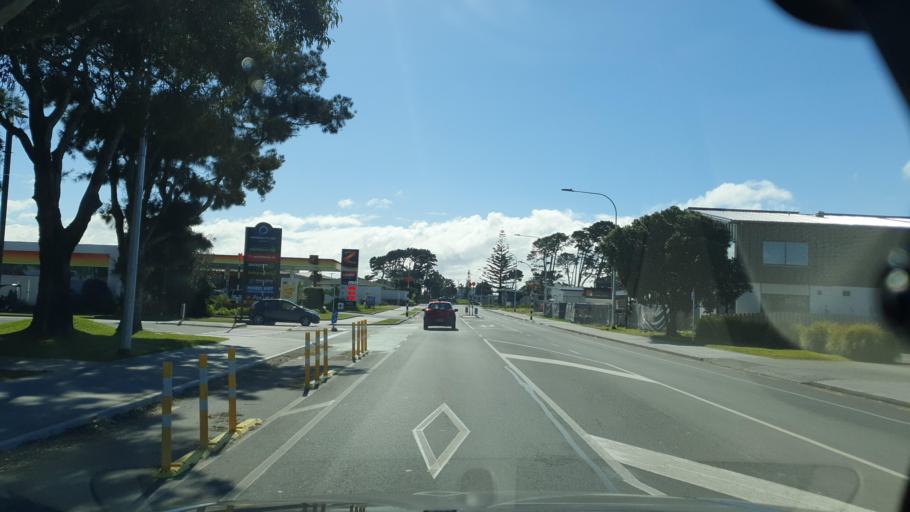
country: NZ
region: Bay of Plenty
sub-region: Tauranga City
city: Tauranga
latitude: -37.6999
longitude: 176.2847
